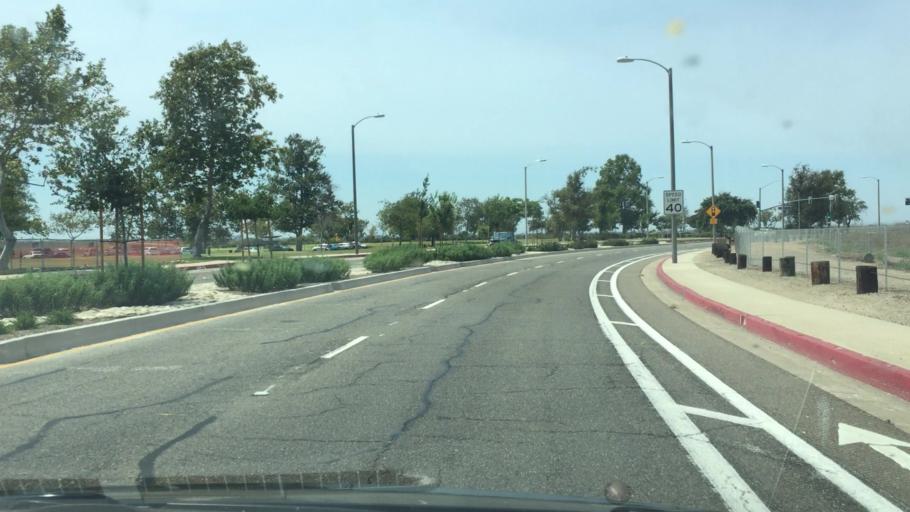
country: US
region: California
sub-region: Orange County
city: Costa Mesa
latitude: 33.6618
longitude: -117.9373
